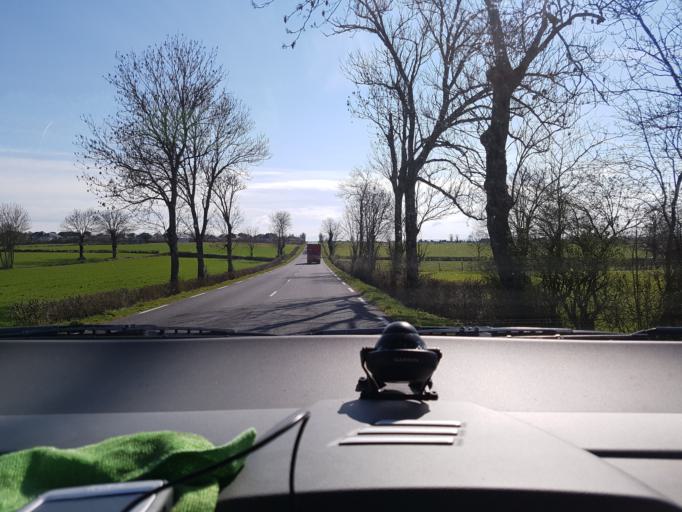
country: FR
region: Midi-Pyrenees
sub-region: Departement de l'Aveyron
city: Druelle
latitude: 44.3693
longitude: 2.5063
